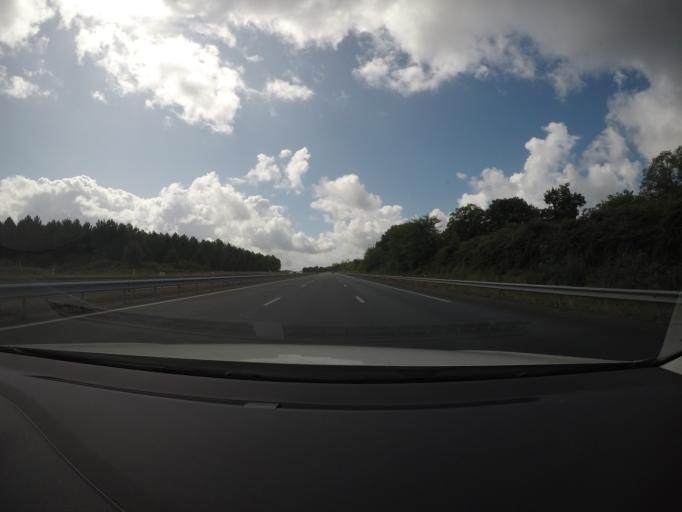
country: FR
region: Aquitaine
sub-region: Departement des Landes
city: Onesse-Laharie
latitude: 44.0389
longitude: -1.0151
